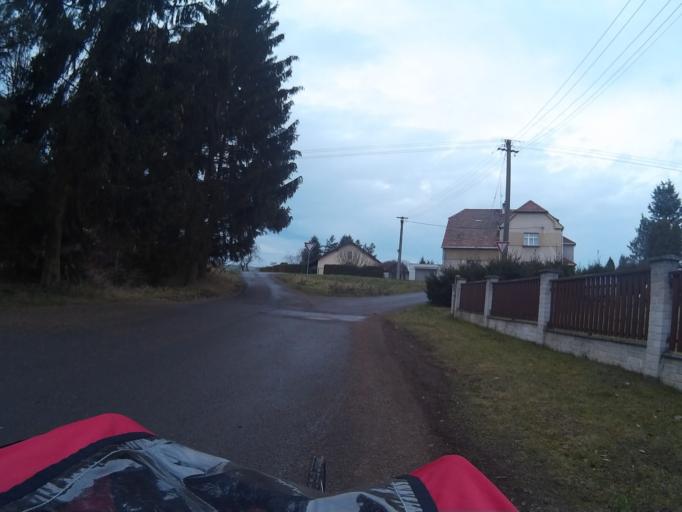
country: CZ
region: Plzensky
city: St'ahlavy
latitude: 49.6696
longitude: 13.4972
